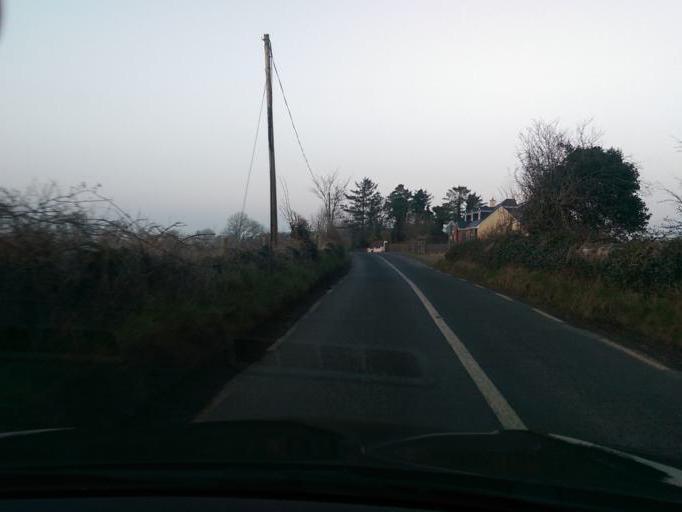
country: IE
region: Connaught
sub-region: County Galway
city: Athenry
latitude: 53.2381
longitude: -8.6622
